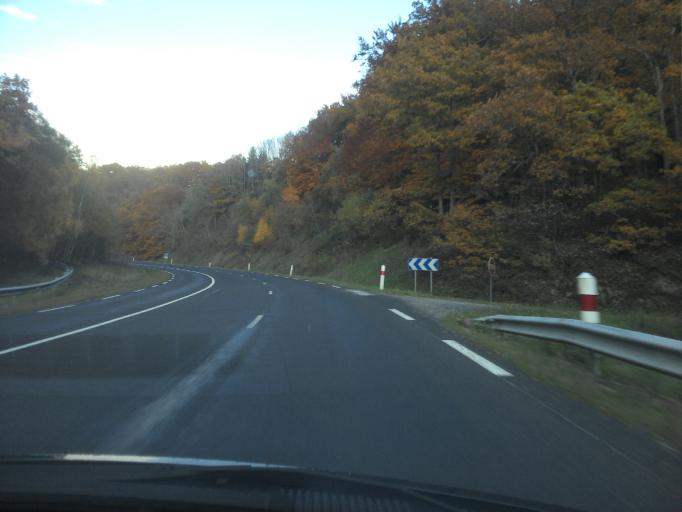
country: FR
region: Auvergne
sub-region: Departement du Puy-de-Dome
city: Gelles
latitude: 45.8392
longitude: 2.7479
